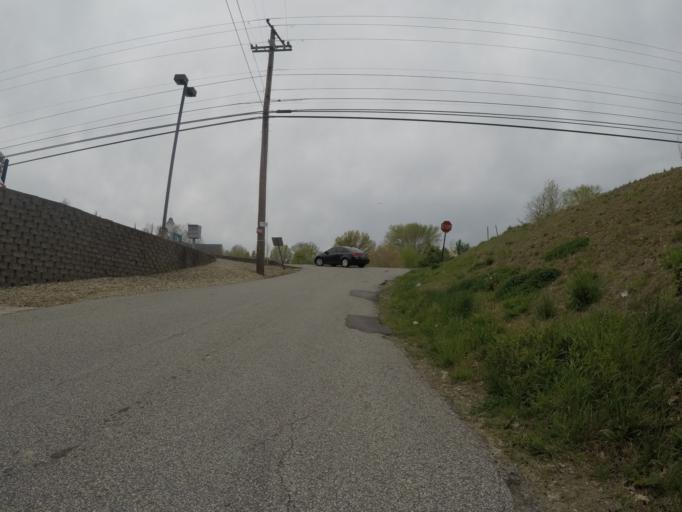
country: US
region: West Virginia
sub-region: Cabell County
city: Pea Ridge
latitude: 38.4113
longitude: -82.3367
